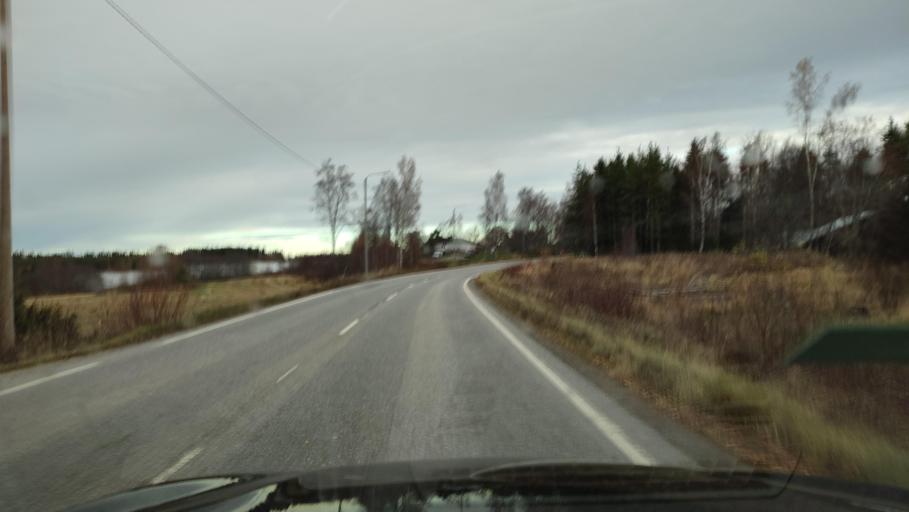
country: FI
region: Ostrobothnia
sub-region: Sydosterbotten
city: Naerpes
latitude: 62.4185
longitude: 21.3429
